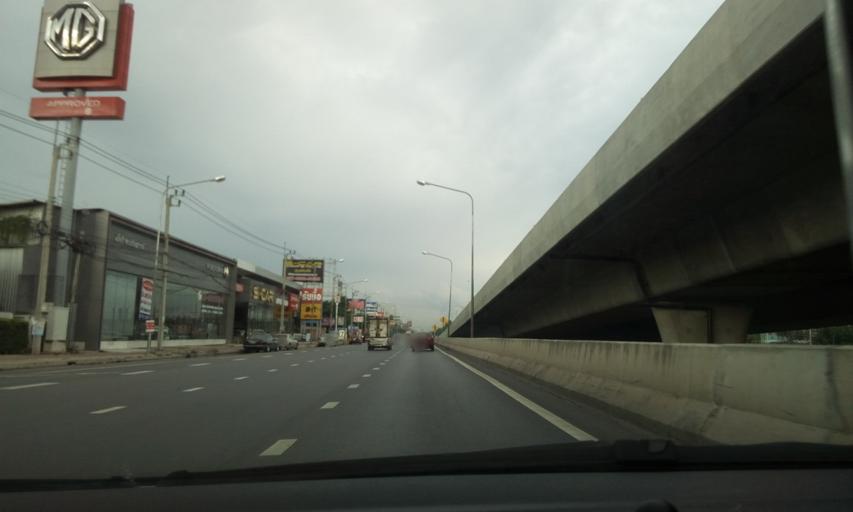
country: TH
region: Nonthaburi
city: Bang Bua Thong
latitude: 13.9270
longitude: 100.4583
